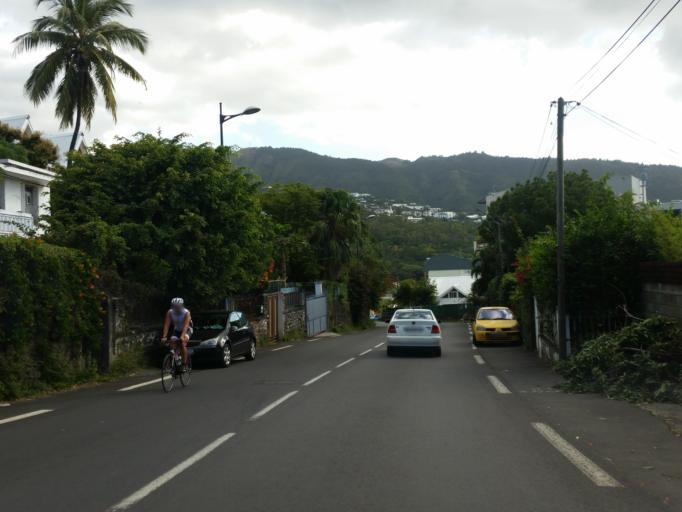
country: RE
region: Reunion
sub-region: Reunion
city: Saint-Denis
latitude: -20.8976
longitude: 55.4622
